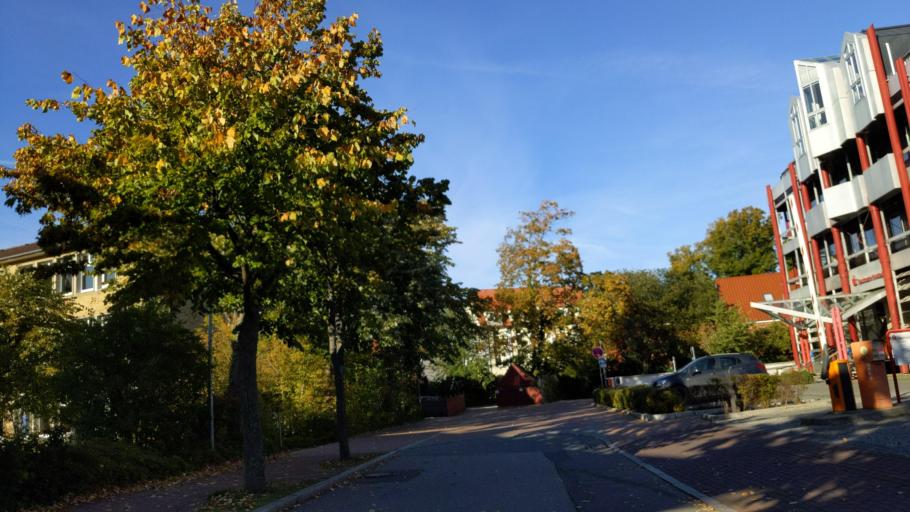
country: DE
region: Schleswig-Holstein
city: Eutin
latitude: 54.1376
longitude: 10.6143
